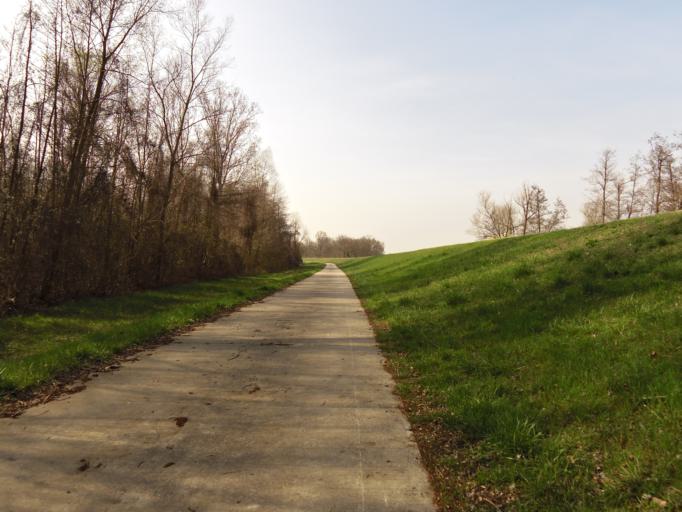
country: DE
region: Hesse
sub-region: Regierungsbezirk Darmstadt
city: Gross-Rohrheim
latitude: 49.7271
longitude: 8.4818
